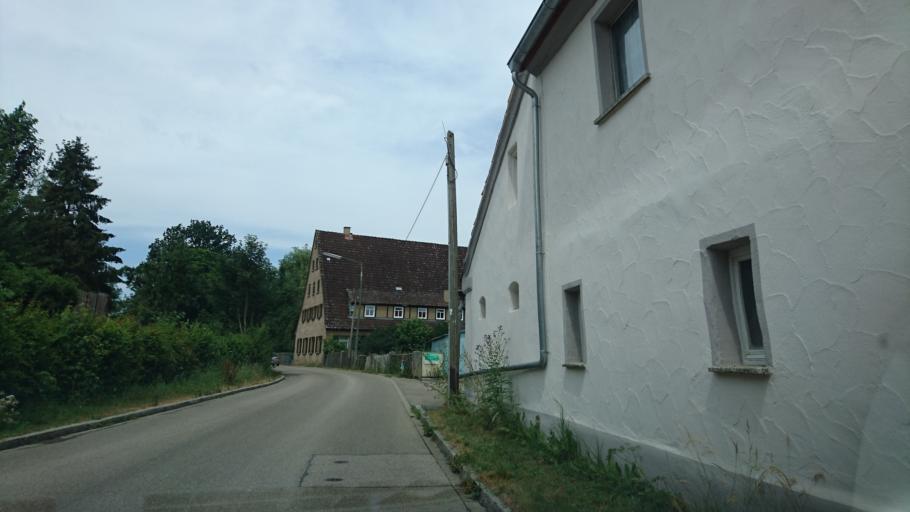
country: DE
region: Bavaria
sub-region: Regierungsbezirk Mittelfranken
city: Roth
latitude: 49.1901
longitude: 11.1072
